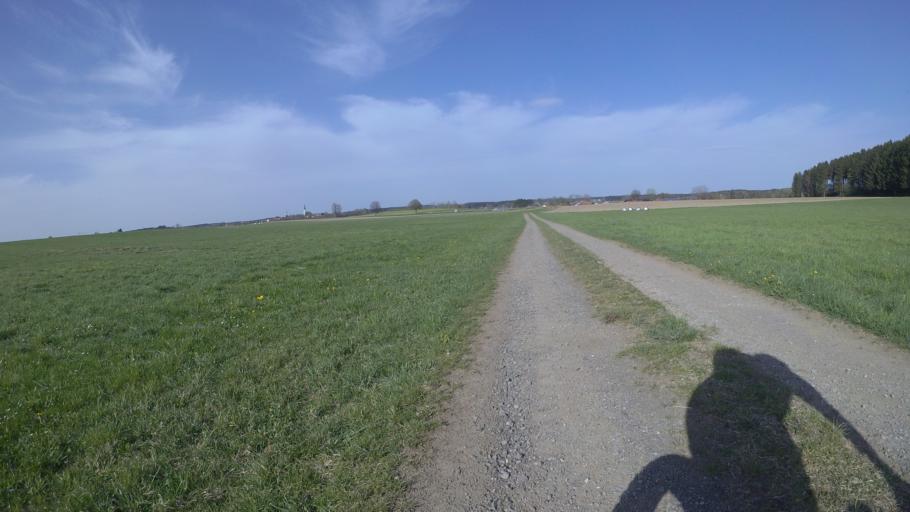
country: DE
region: Bavaria
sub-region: Upper Bavaria
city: Nussdorf
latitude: 47.9254
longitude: 12.5970
